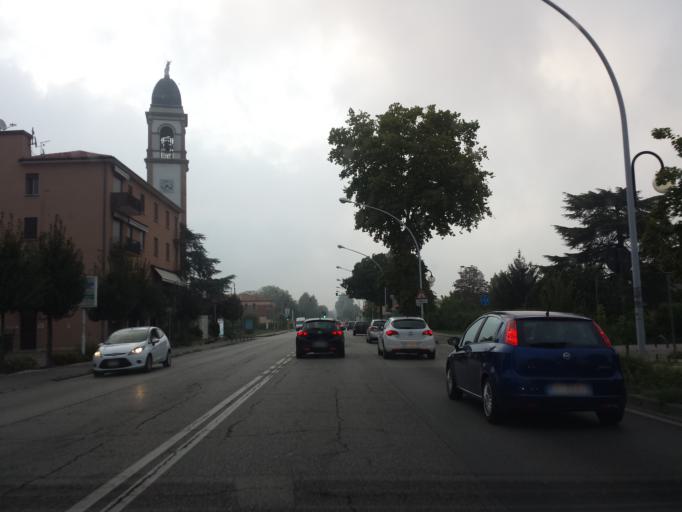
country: IT
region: Veneto
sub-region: Provincia di Padova
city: Caselle
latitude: 45.4147
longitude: 11.8349
